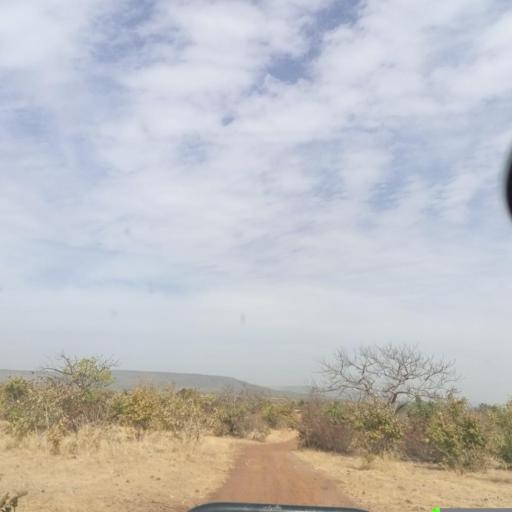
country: ML
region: Koulikoro
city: Koulikoro
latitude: 13.1610
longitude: -7.7270
